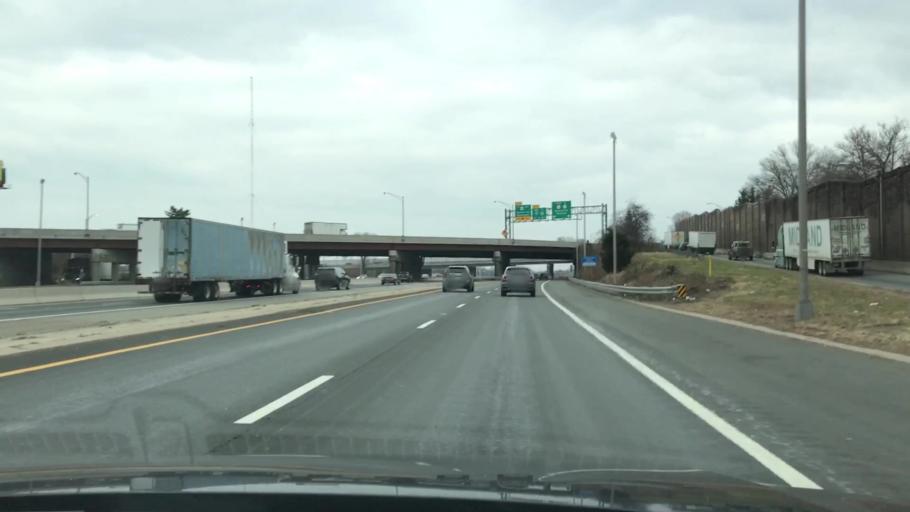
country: US
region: New Jersey
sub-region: Bergen County
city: Hackensack
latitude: 40.8753
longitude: -74.0618
